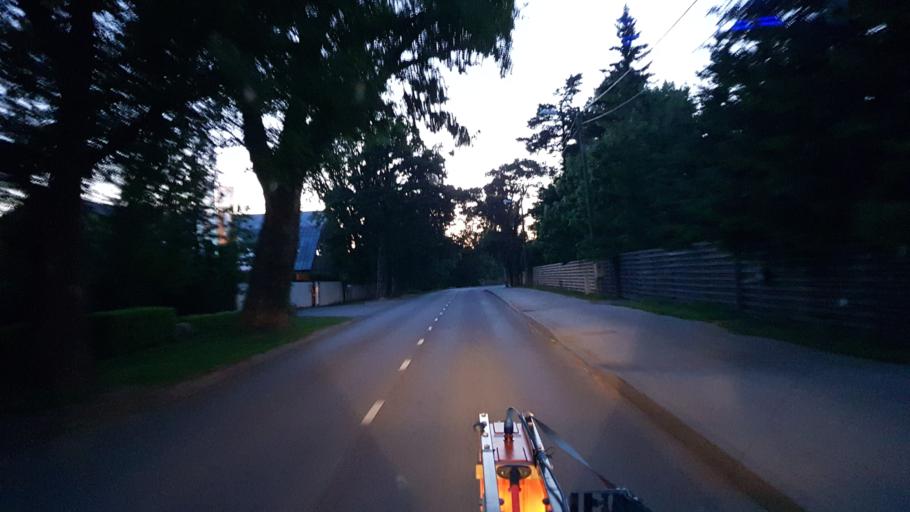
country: EE
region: Harju
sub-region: Harku vald
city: Tabasalu
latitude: 59.4446
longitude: 24.5924
